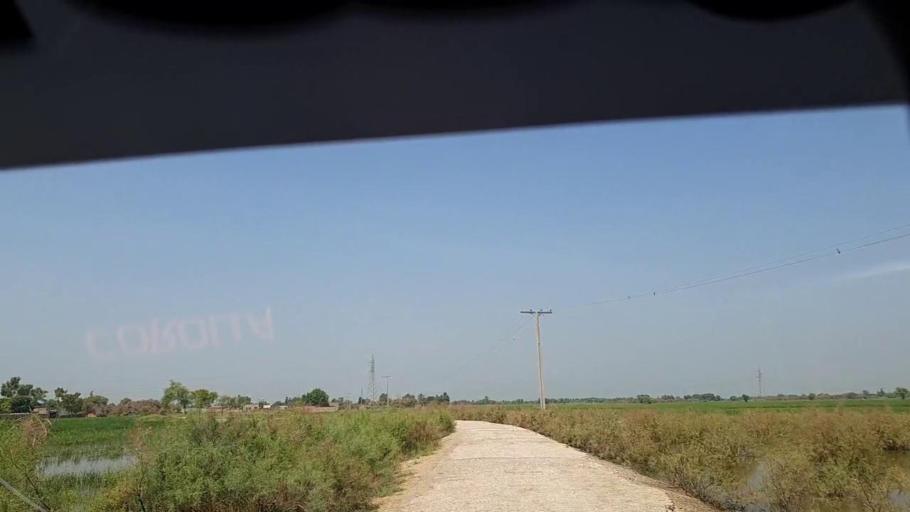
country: PK
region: Sindh
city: Ghauspur
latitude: 28.1718
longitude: 69.0691
